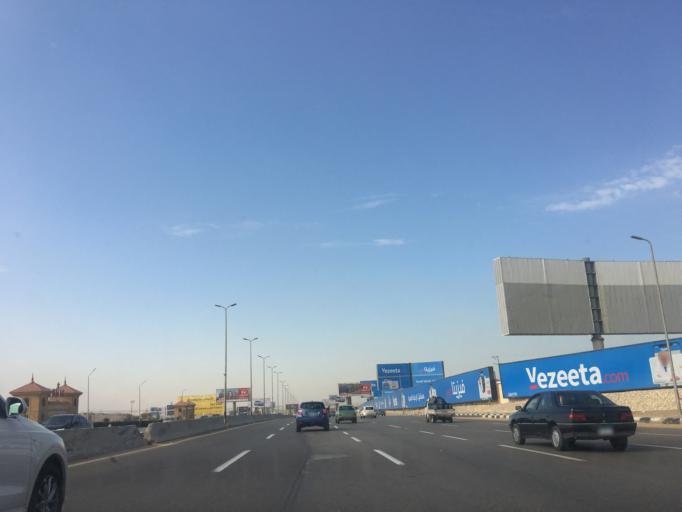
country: EG
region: Muhafazat al Qahirah
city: Cairo
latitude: 30.0230
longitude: 31.3671
